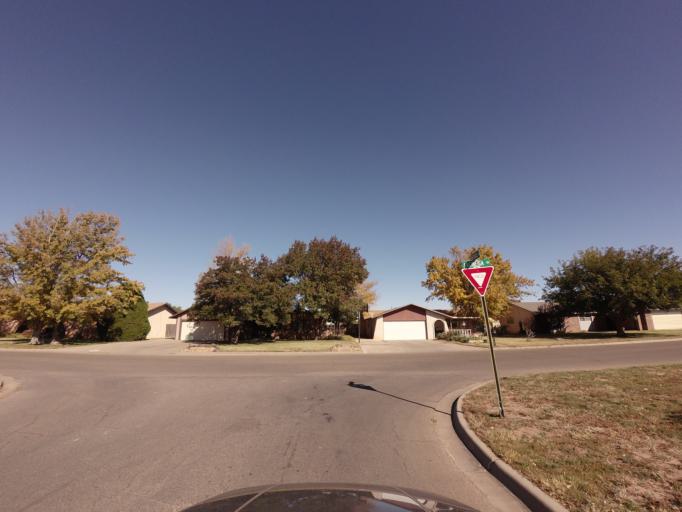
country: US
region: New Mexico
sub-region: Curry County
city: Clovis
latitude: 34.4260
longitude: -103.1872
